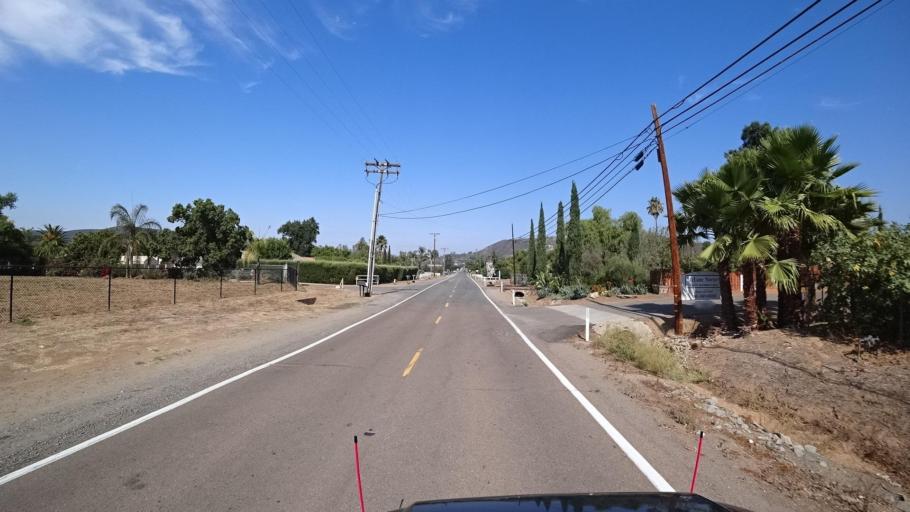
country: US
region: California
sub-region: San Diego County
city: San Marcos
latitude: 33.1786
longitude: -117.1490
